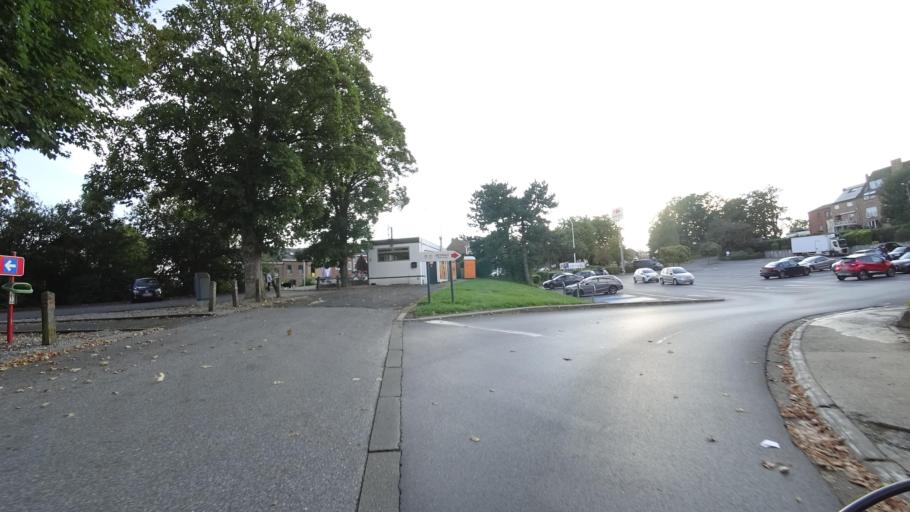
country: BE
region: Wallonia
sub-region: Province de Namur
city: Namur
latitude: 50.4730
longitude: 4.8176
